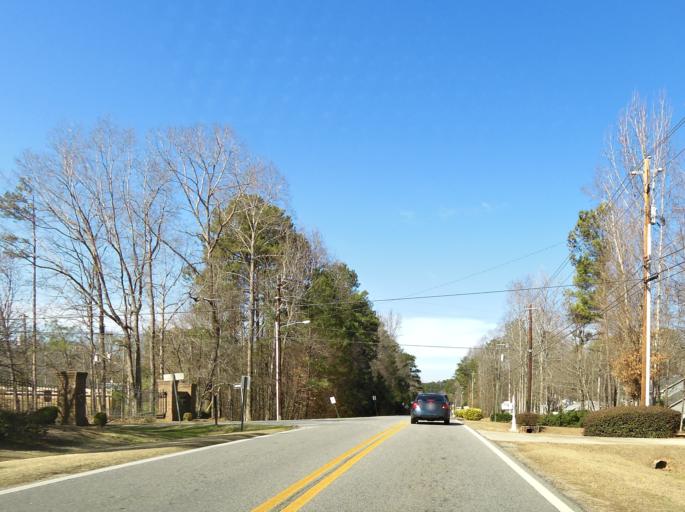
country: US
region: Georgia
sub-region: Bibb County
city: West Point
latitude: 32.8632
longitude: -83.7535
